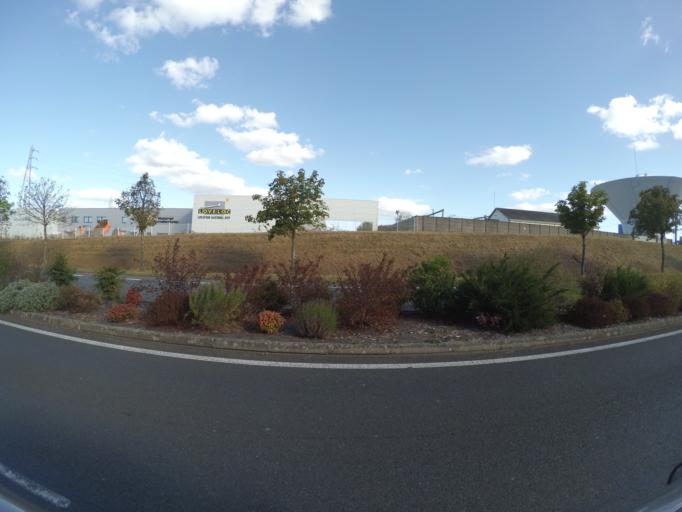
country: FR
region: Pays de la Loire
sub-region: Departement de Maine-et-Loire
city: Mazieres-en-Mauges
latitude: 47.0682
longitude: -0.8422
